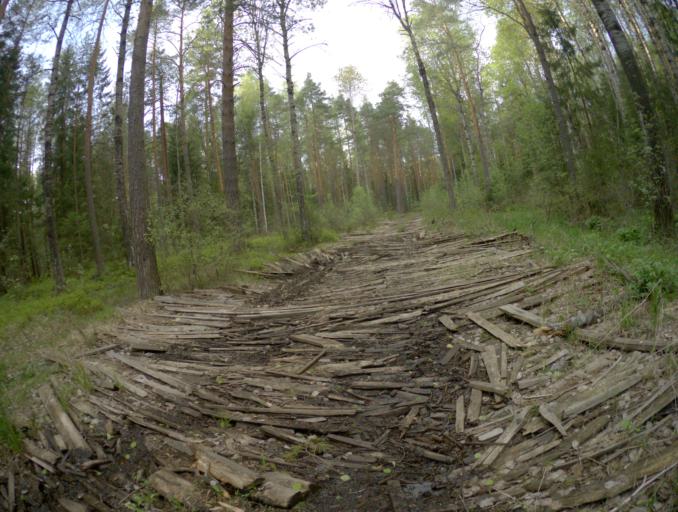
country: RU
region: Vladimir
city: Anopino
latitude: 55.7202
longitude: 40.6132
